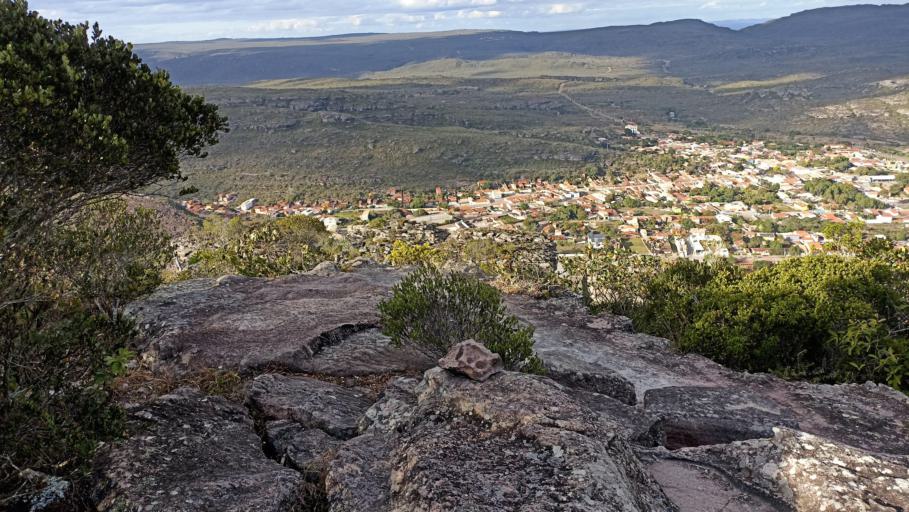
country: BR
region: Bahia
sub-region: Andarai
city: Vera Cruz
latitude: -13.0092
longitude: -41.3798
